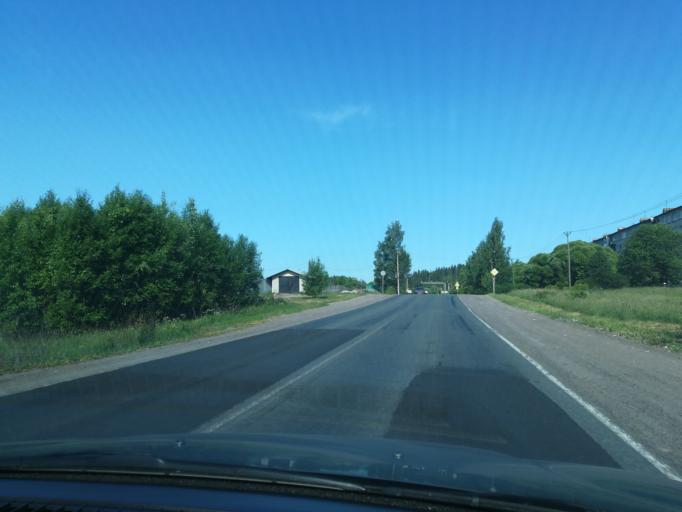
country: RU
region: Leningrad
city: Lesogorskiy
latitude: 61.0872
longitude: 28.9055
